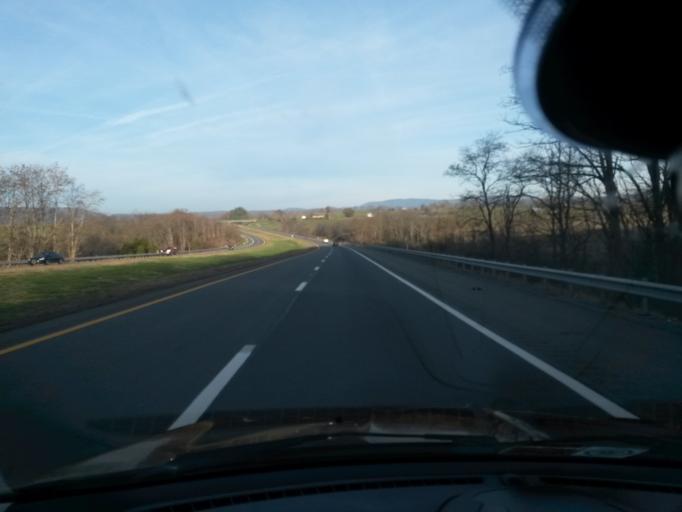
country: US
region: West Virginia
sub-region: Greenbrier County
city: Lewisburg
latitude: 37.8381
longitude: -80.4625
